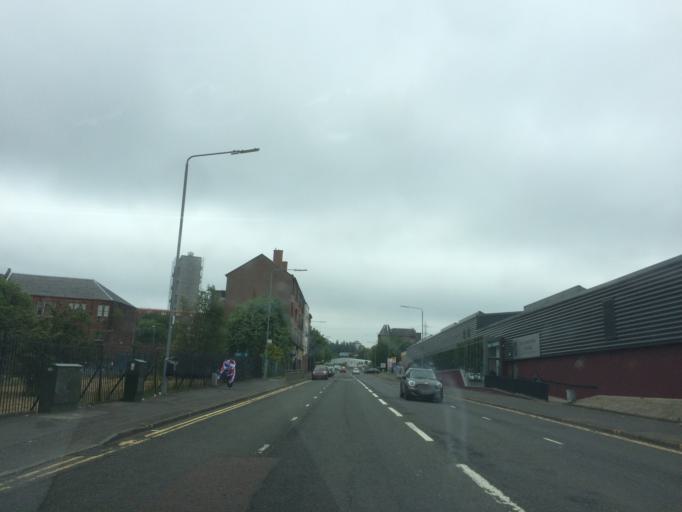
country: GB
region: Scotland
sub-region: Glasgow City
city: Glasgow
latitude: 55.8717
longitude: -4.2608
